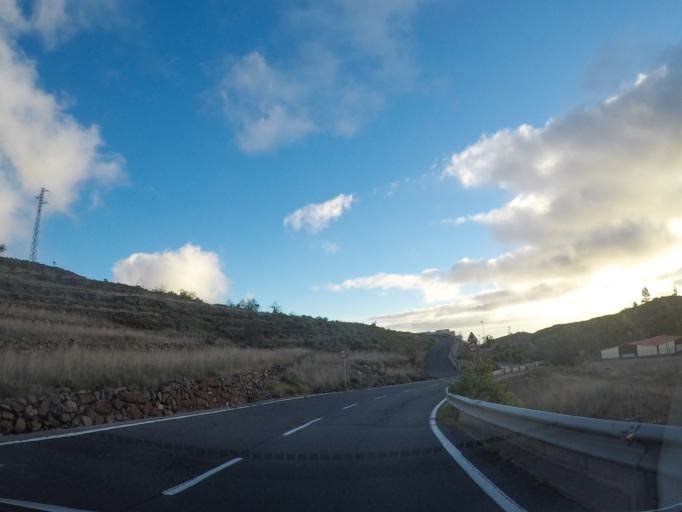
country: ES
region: Canary Islands
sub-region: Provincia de Santa Cruz de Tenerife
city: Alajero
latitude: 28.0713
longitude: -17.2376
